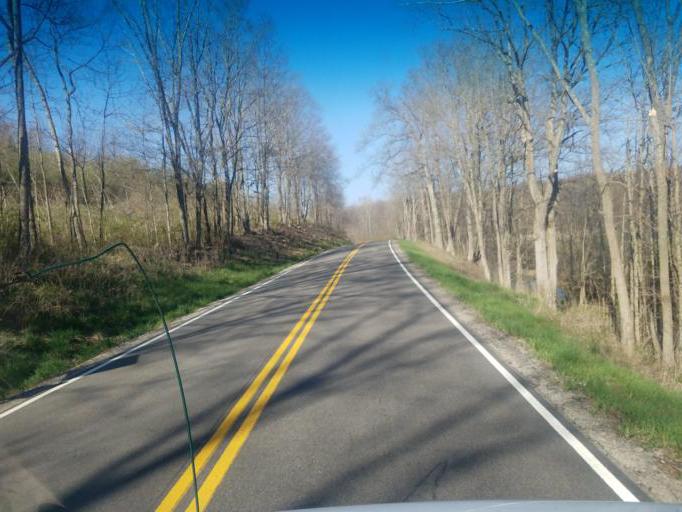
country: US
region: Ohio
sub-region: Muskingum County
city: Frazeysburg
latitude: 40.2797
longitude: -82.0932
